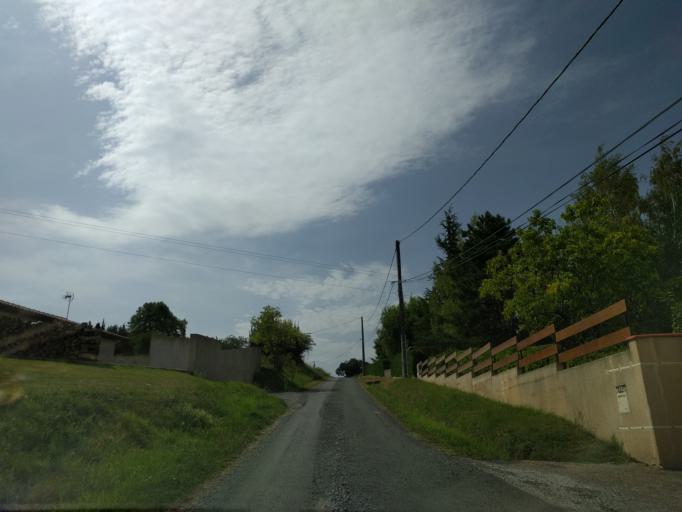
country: FR
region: Midi-Pyrenees
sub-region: Departement du Tarn
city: Castres
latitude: 43.6400
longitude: 2.2073
